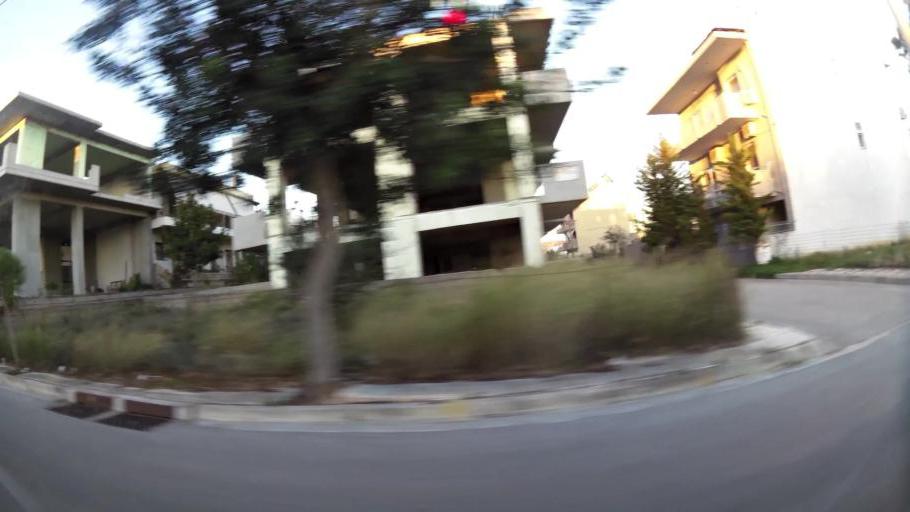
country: GR
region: Attica
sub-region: Nomarchia Dytikis Attikis
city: Ano Liosia
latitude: 38.0878
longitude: 23.6965
